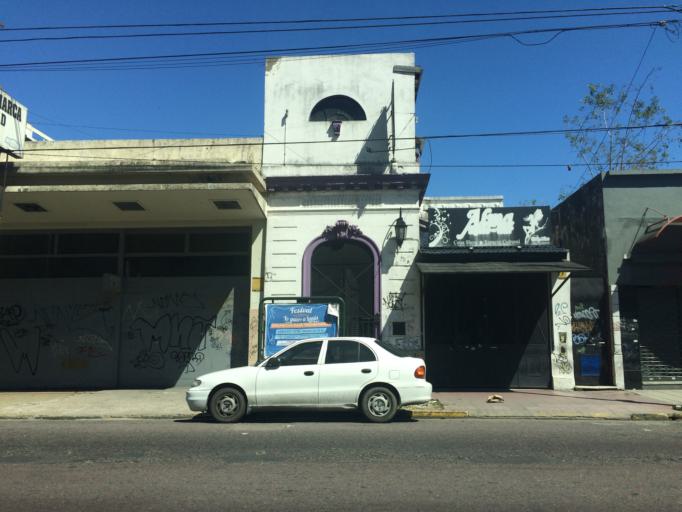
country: AR
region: Buenos Aires
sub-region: Partido de Lanus
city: Lanus
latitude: -34.7303
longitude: -58.3964
